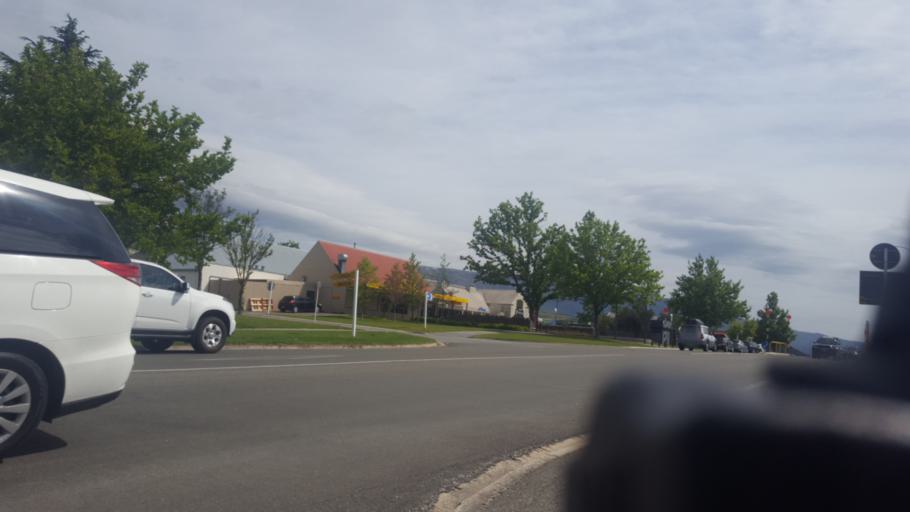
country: NZ
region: Otago
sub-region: Queenstown-Lakes District
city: Wanaka
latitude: -45.0378
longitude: 169.1987
